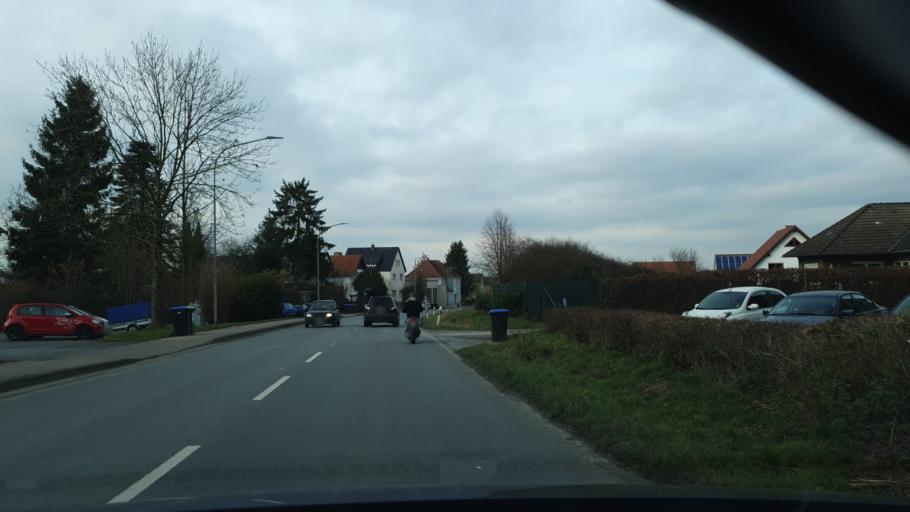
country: DE
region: North Rhine-Westphalia
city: Spenge
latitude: 52.1349
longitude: 8.4843
